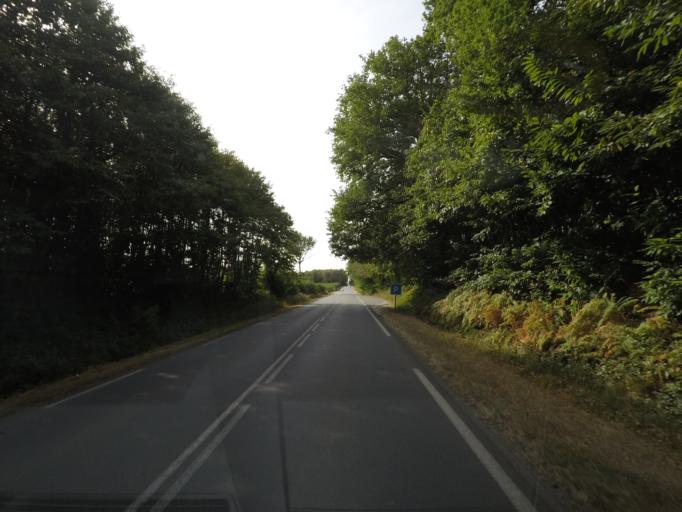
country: FR
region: Poitou-Charentes
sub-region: Departement des Deux-Sevres
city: Chef-Boutonne
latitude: 46.1831
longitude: -0.0323
